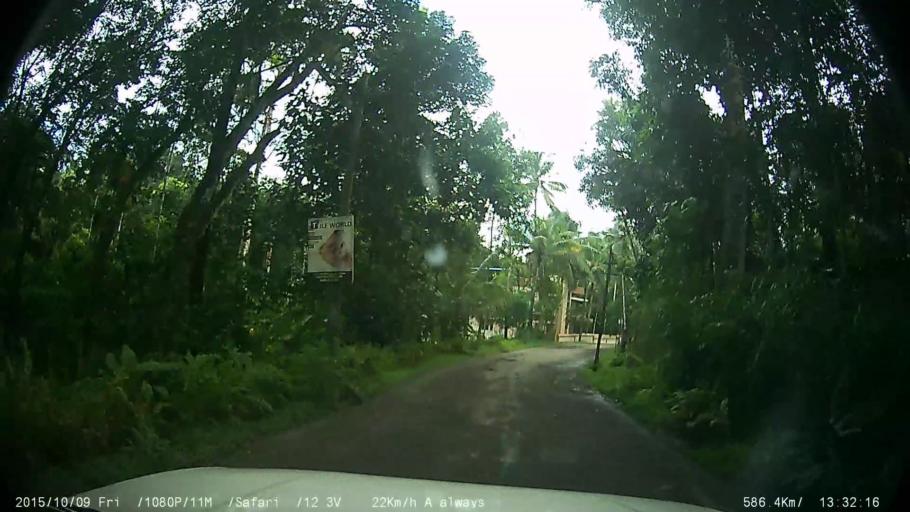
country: IN
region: Kerala
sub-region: Ernakulam
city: Ramamangalam
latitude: 9.9116
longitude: 76.5582
